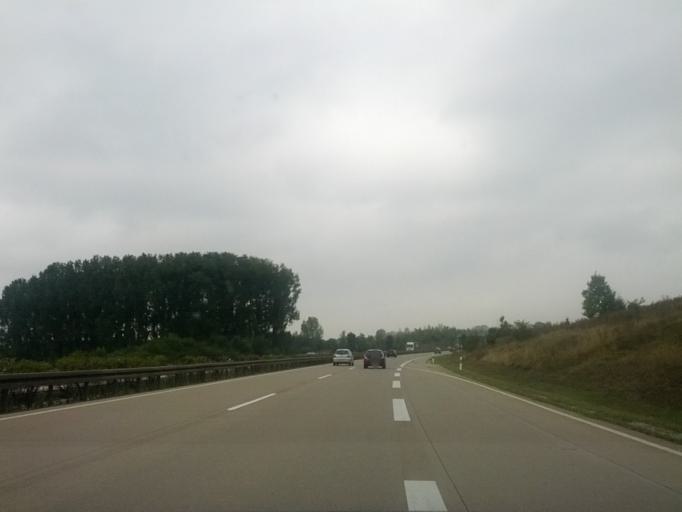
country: DE
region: Thuringia
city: Ingersleben
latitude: 50.8976
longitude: 10.9491
